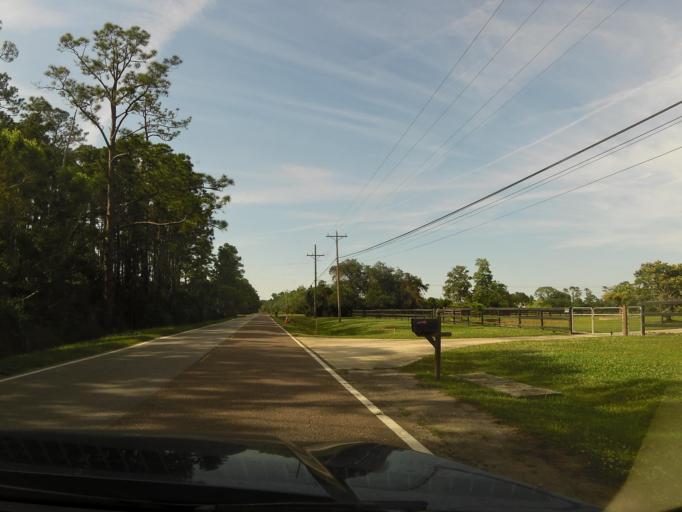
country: US
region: Florida
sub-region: Duval County
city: Atlantic Beach
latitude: 30.4664
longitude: -81.4698
